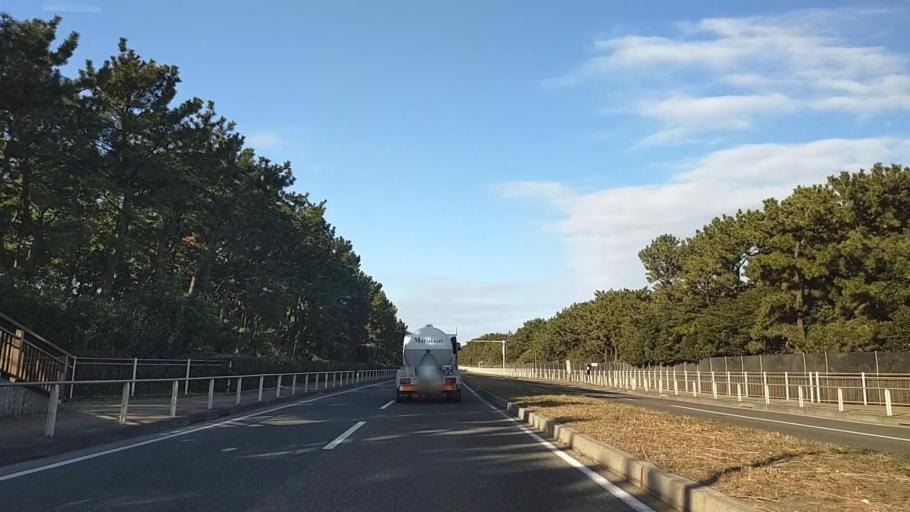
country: JP
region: Kanagawa
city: Chigasaki
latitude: 35.3181
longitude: 139.4148
